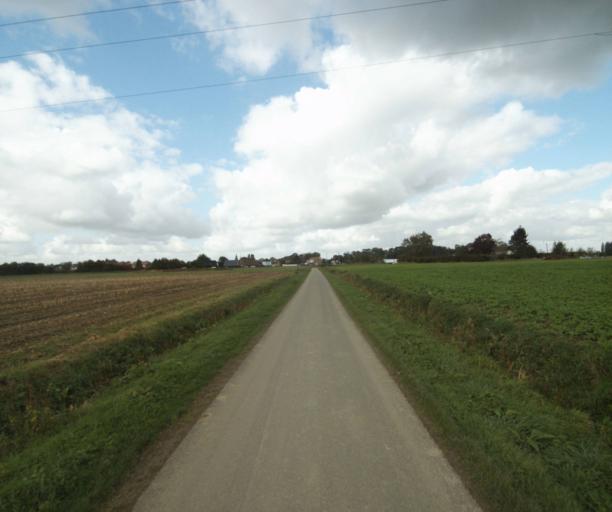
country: FR
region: Nord-Pas-de-Calais
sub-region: Departement du Nord
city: Frelinghien
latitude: 50.7092
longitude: 2.9423
